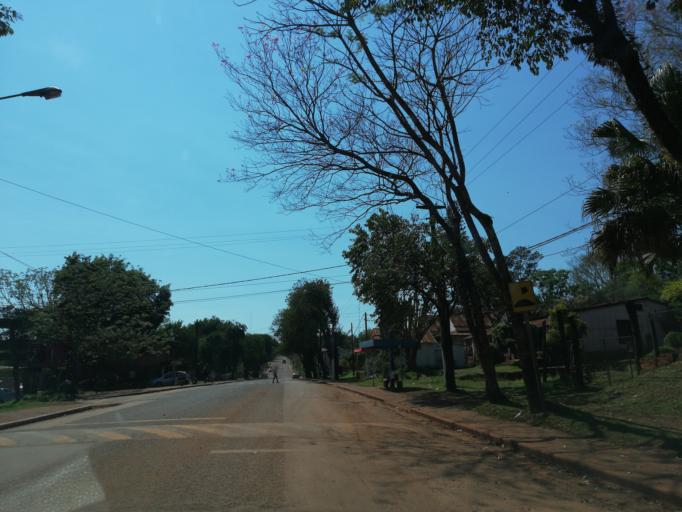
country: AR
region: Misiones
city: Puerto Eldorado
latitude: -26.4108
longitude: -54.6805
